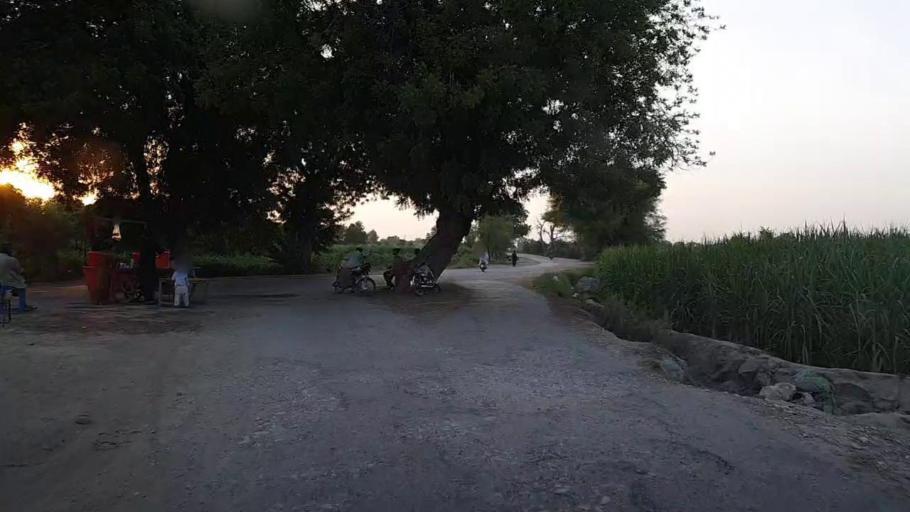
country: PK
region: Sindh
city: Ubauro
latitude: 28.3028
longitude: 69.7940
